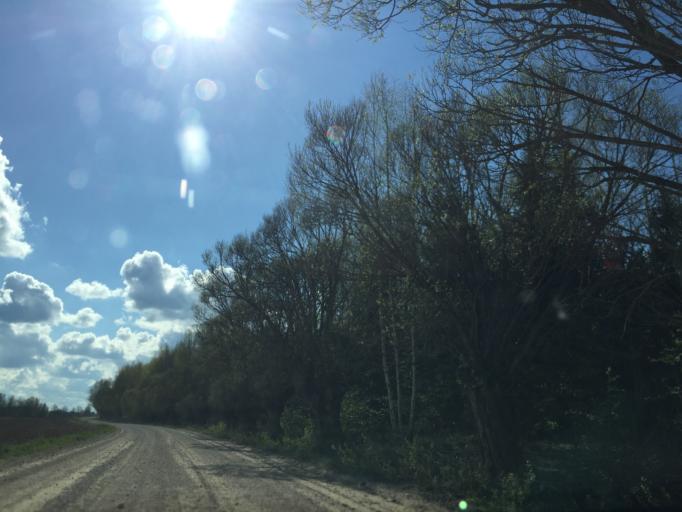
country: LV
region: Beverina
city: Murmuiza
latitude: 57.4855
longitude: 25.6304
